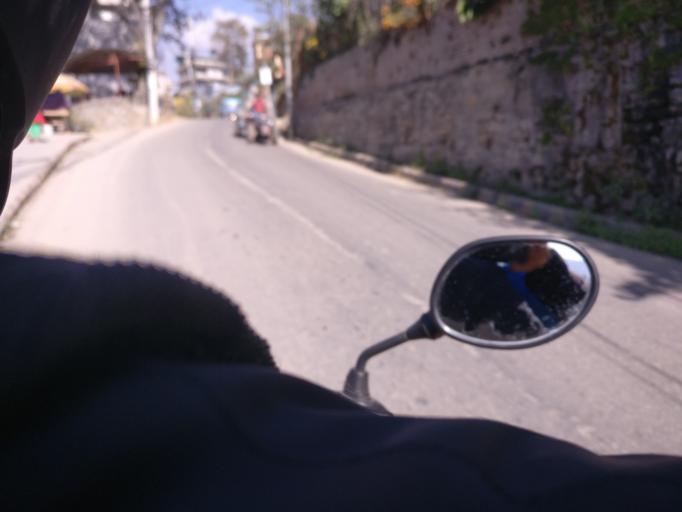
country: NP
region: Central Region
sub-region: Bagmati Zone
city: Patan
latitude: 27.6538
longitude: 85.3146
